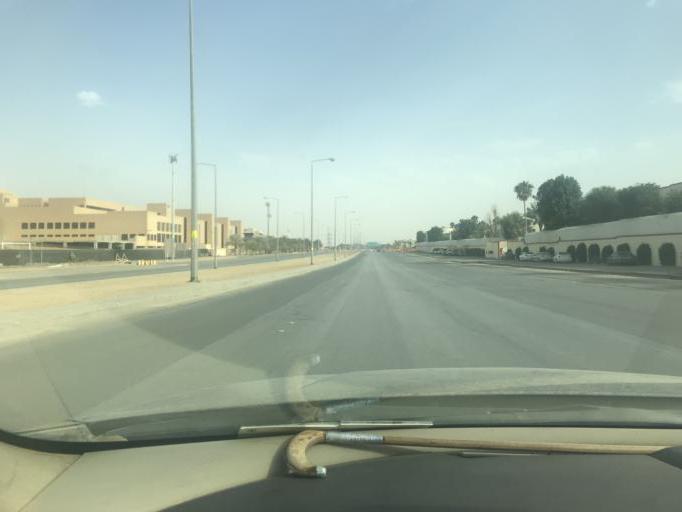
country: SA
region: Ar Riyad
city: Riyadh
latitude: 24.8122
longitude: 46.6905
